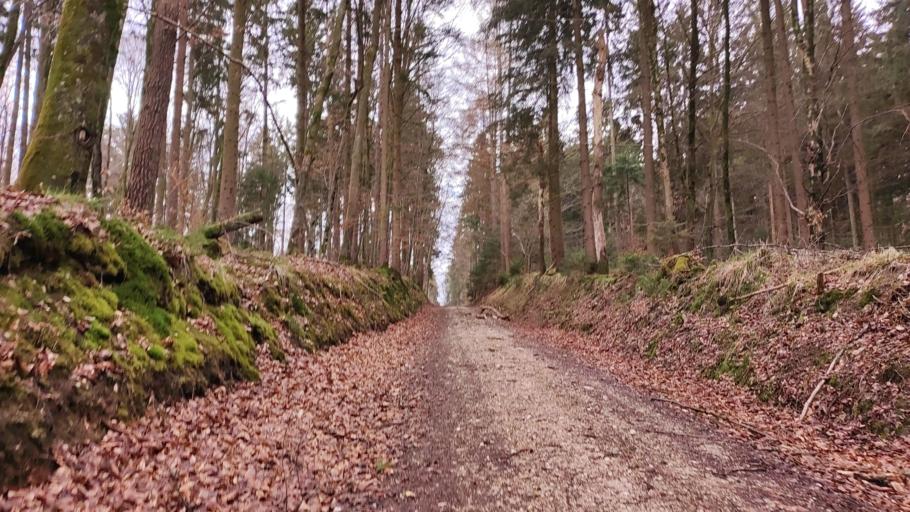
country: DE
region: Bavaria
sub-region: Swabia
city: Landensberg
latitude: 48.4330
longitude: 10.5561
